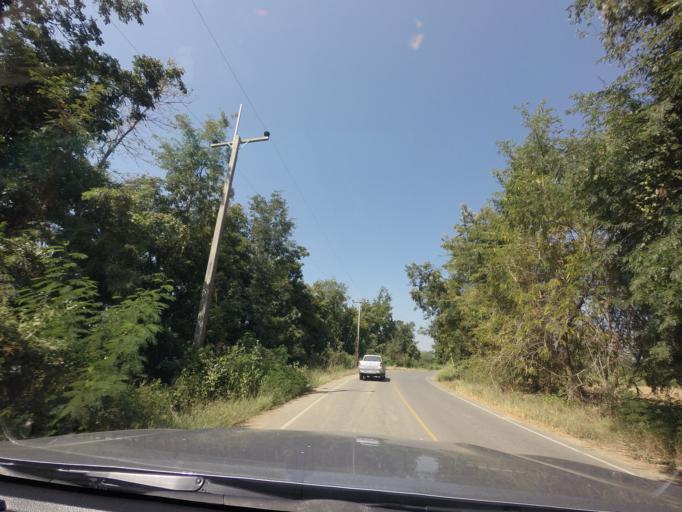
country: TH
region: Sukhothai
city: Si Samrong
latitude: 17.1278
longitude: 99.7817
